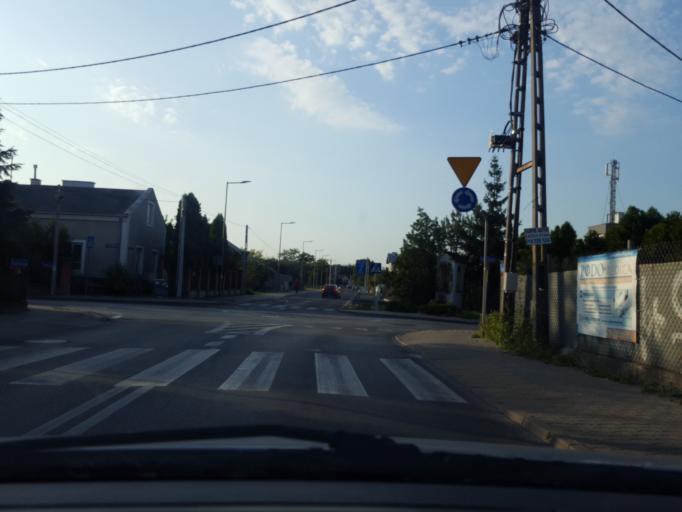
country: PL
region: Masovian Voivodeship
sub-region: Warszawa
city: Rembertow
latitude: 52.2703
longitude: 21.1504
